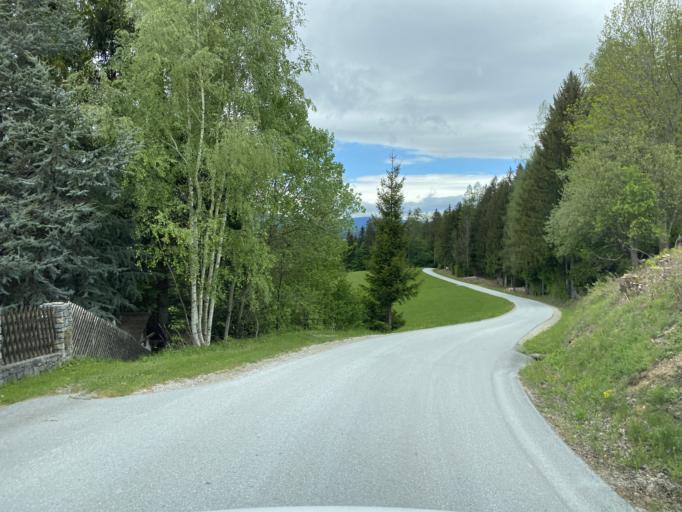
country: AT
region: Styria
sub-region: Politischer Bezirk Weiz
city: Baierdorf-Umgebung
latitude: 47.3040
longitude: 15.7007
